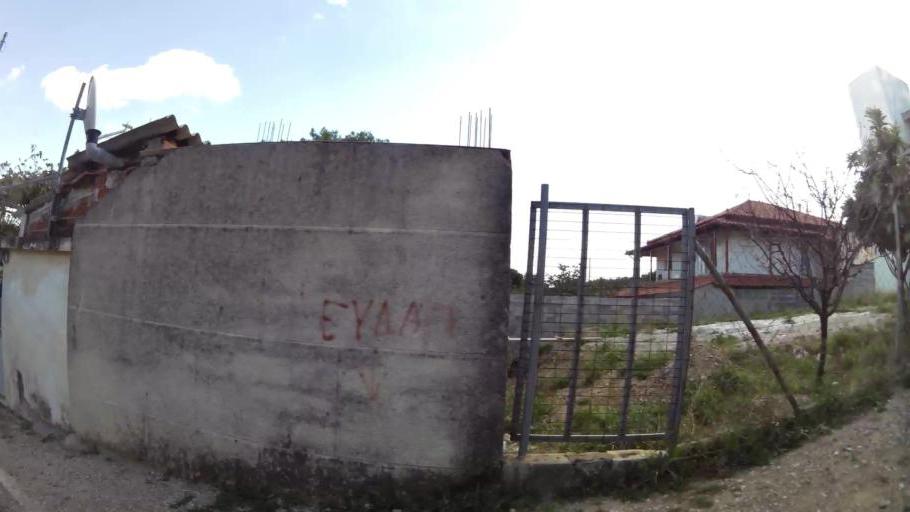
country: GR
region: Attica
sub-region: Nomarchia Anatolikis Attikis
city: Thrakomakedones
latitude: 38.1176
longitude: 23.7245
